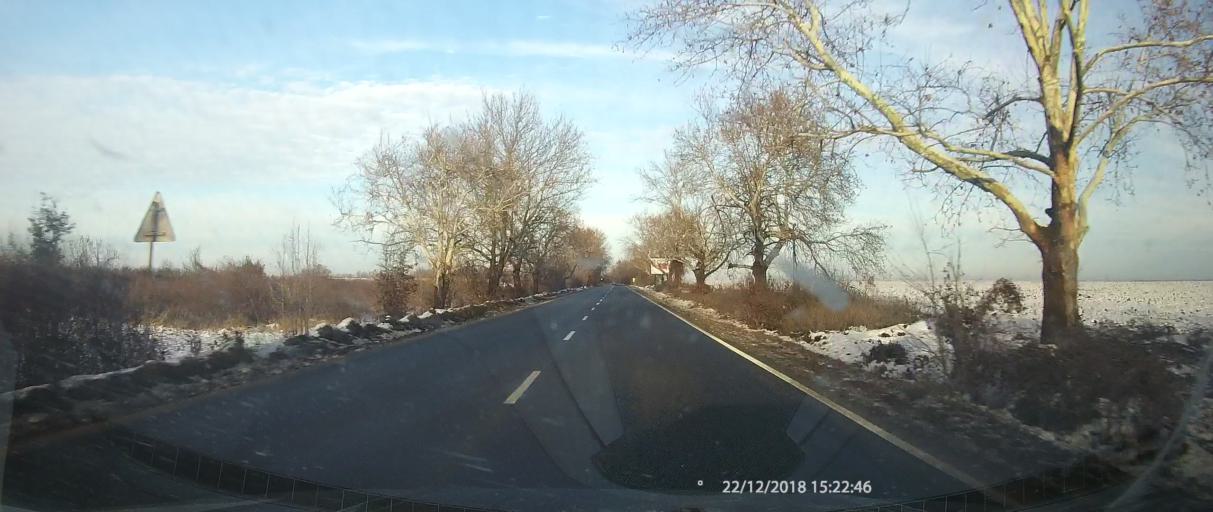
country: BG
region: Ruse
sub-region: Obshtina Ivanovo
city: Ivanovo
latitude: 43.7085
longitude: 25.9168
